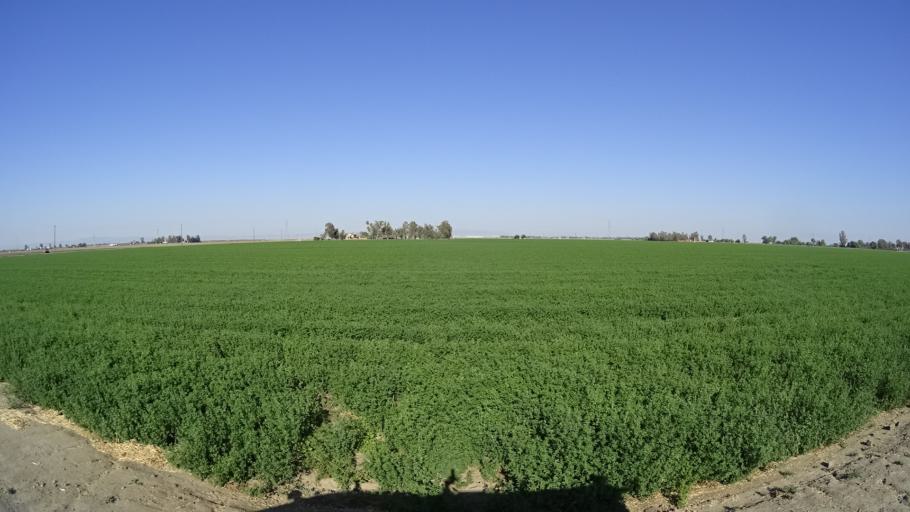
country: US
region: California
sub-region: Kings County
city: Lemoore Station
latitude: 36.3300
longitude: -119.8784
